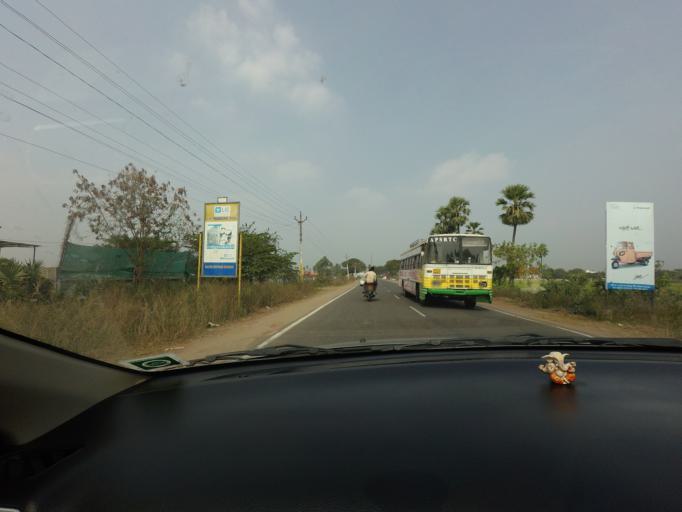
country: IN
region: Andhra Pradesh
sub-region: Krishna
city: Kankipadu
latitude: 16.4503
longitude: 80.7708
